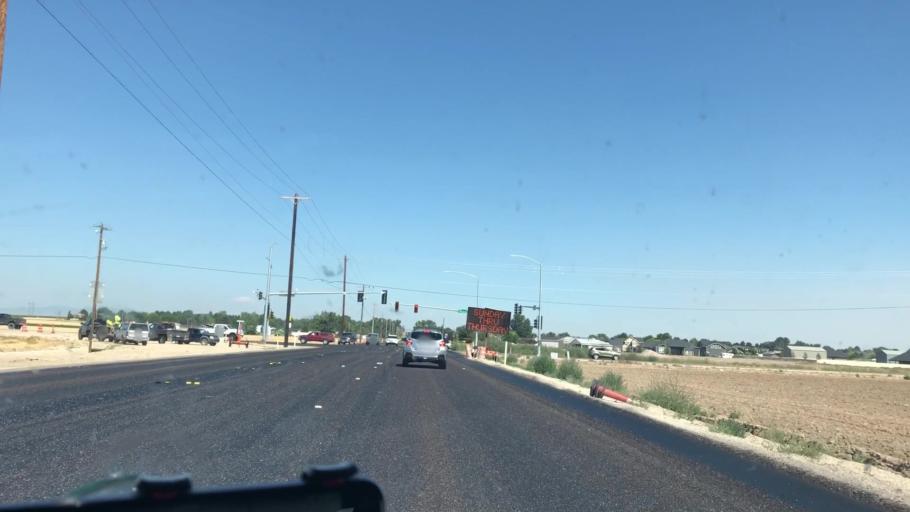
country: US
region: Idaho
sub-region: Canyon County
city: Caldwell
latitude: 43.6039
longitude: -116.7144
